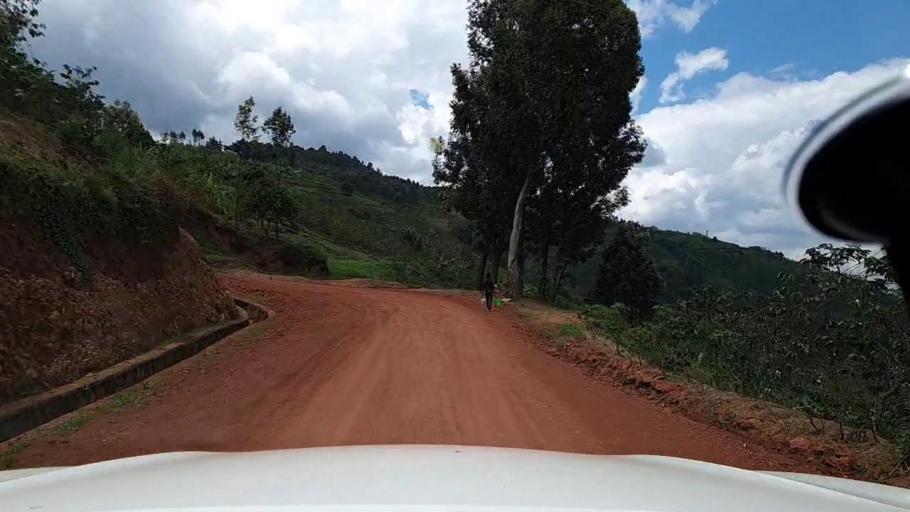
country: RW
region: Northern Province
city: Byumba
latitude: -1.7512
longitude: 29.8444
